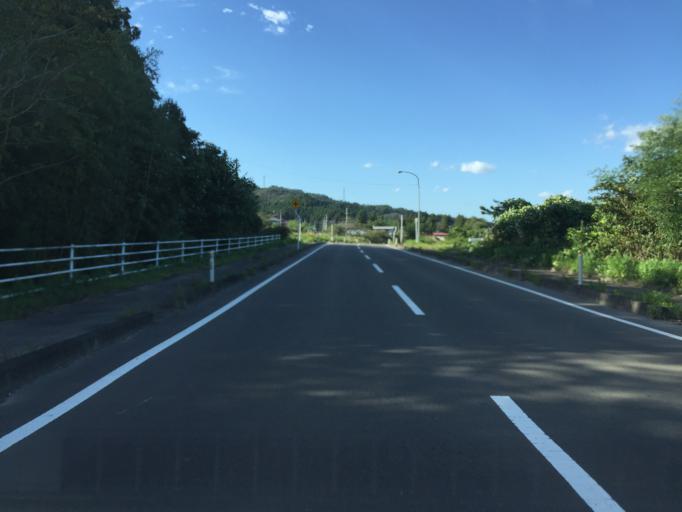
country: JP
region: Miyagi
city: Marumori
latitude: 37.8889
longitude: 140.7727
